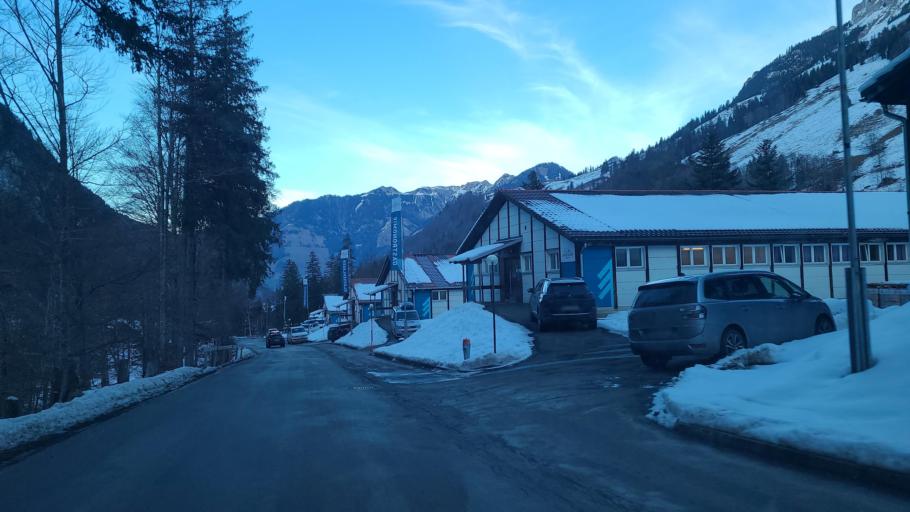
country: CH
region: Obwalden
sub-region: Obwalden
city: Sachseln
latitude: 46.8120
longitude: 8.2820
